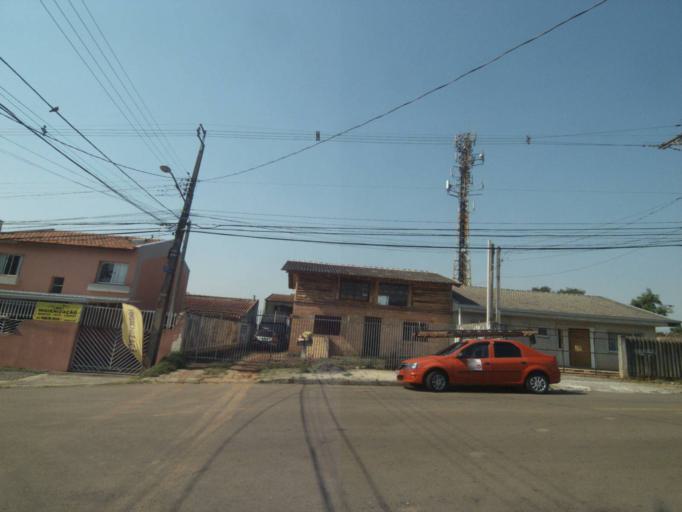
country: BR
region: Parana
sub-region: Sao Jose Dos Pinhais
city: Sao Jose dos Pinhais
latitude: -25.4956
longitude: -49.2638
